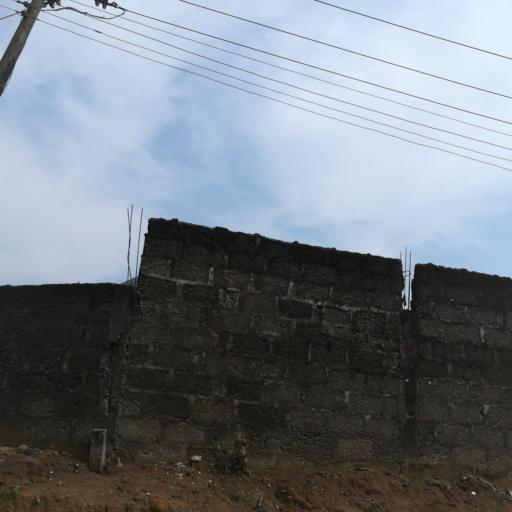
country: NG
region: Rivers
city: Port Harcourt
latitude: 4.8714
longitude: 7.0228
